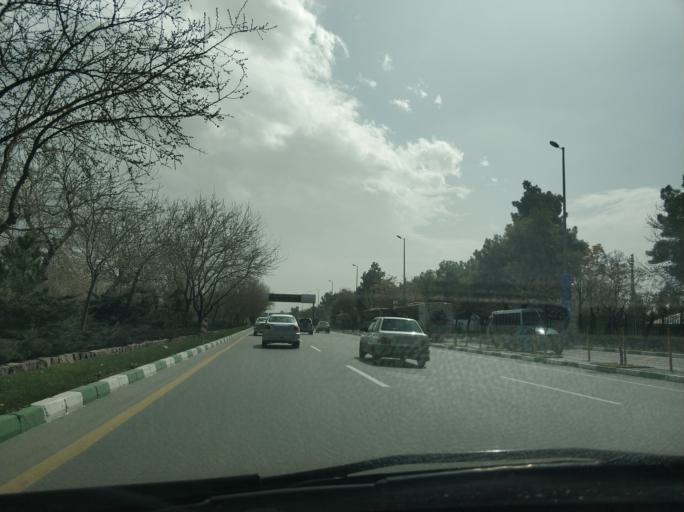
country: IR
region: Razavi Khorasan
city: Mashhad
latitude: 36.3185
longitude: 59.5292
